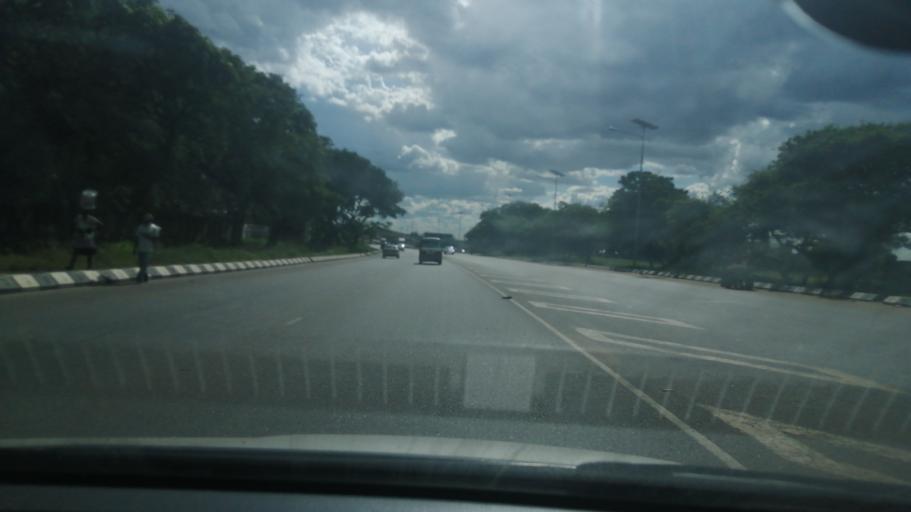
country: ZW
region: Harare
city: Harare
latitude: -17.8502
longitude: 31.0582
